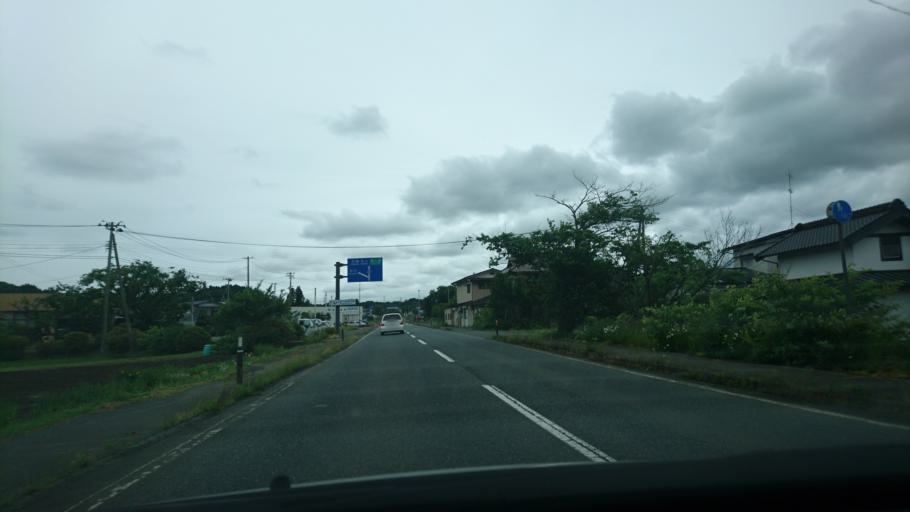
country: JP
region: Iwate
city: Ichinoseki
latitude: 39.0098
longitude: 141.1090
